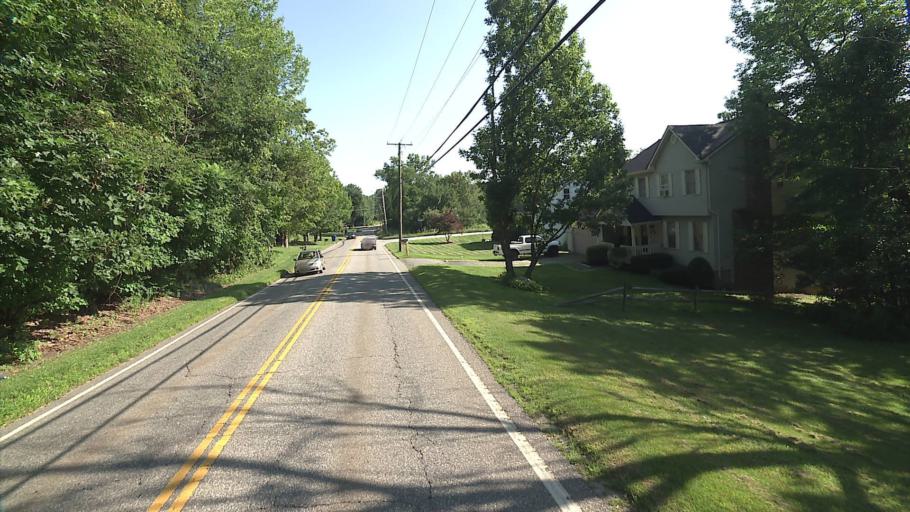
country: US
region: Connecticut
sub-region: Litchfield County
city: Northwest Harwinton
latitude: 41.8140
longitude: -73.0828
